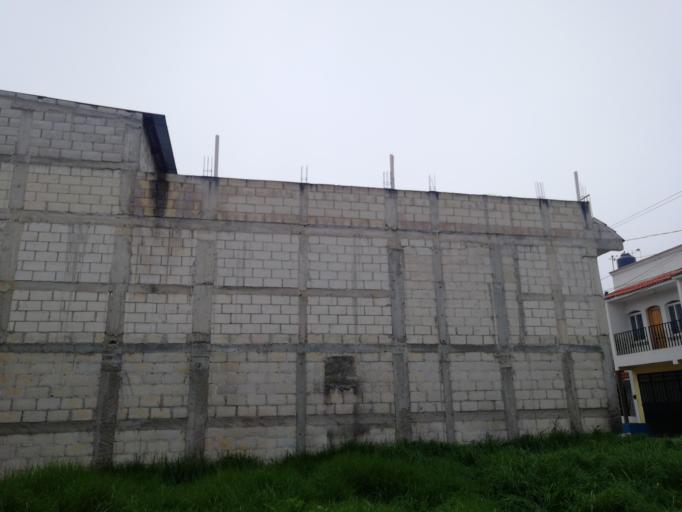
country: GT
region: Quetzaltenango
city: Quetzaltenango
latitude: 14.8547
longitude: -91.5146
